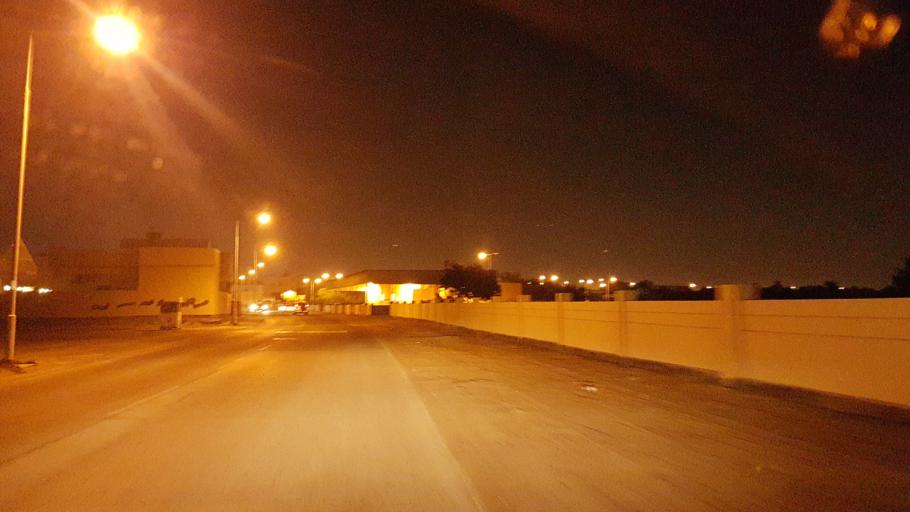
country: BH
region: Manama
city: Jidd Hafs
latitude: 26.2280
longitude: 50.5144
